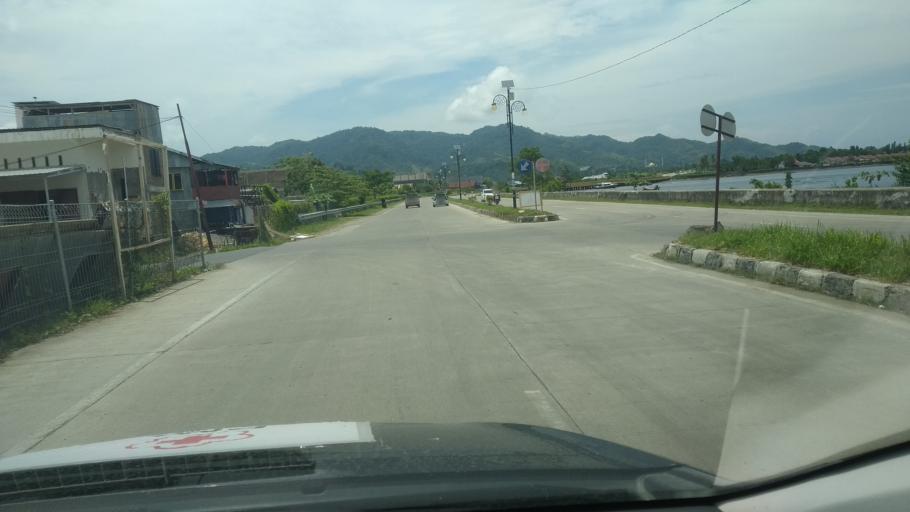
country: ID
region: Sulawesi Barat
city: Mamuju
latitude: -2.6806
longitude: 118.8709
